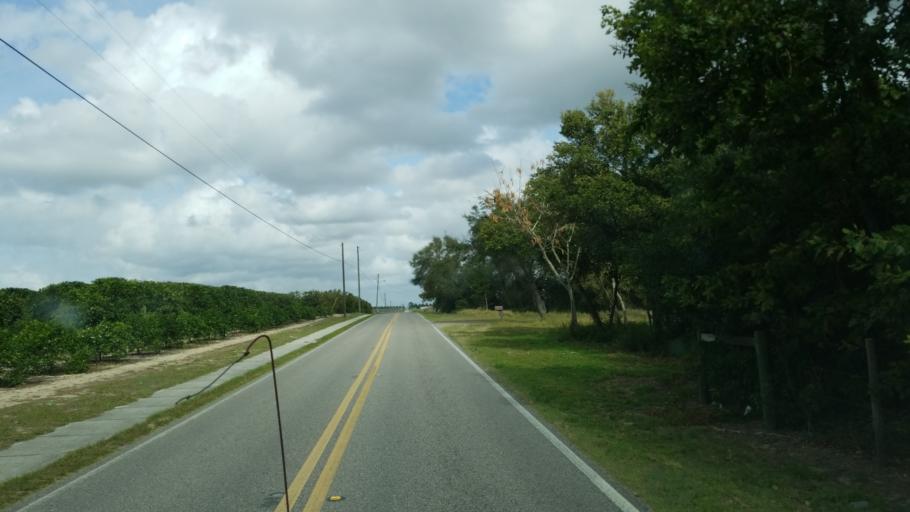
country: US
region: Florida
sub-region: Polk County
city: Dundee
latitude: 28.0304
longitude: -81.6115
